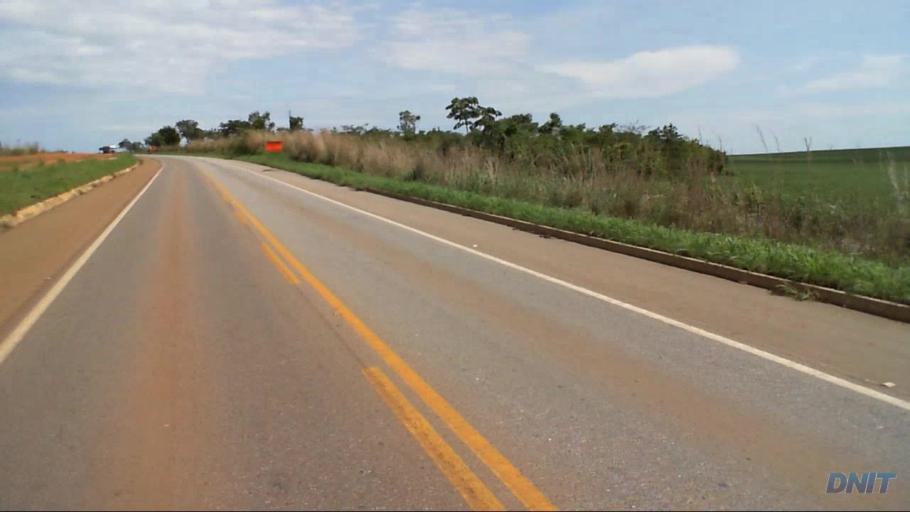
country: BR
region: Goias
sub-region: Barro Alto
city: Barro Alto
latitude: -15.1192
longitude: -48.8379
